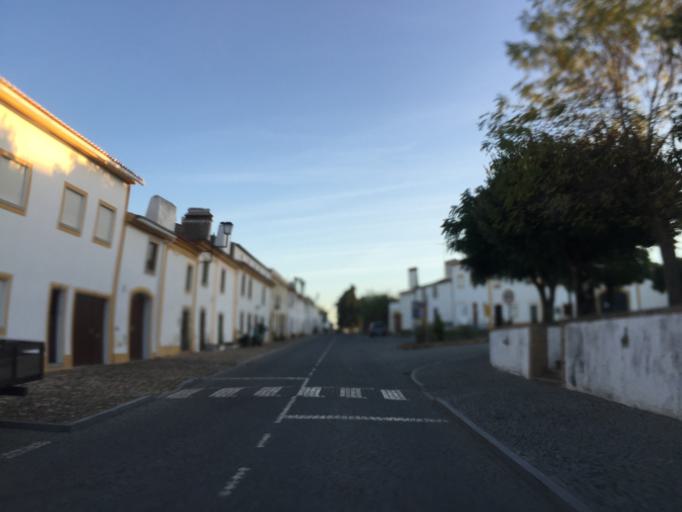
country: PT
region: Portalegre
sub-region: Alter do Chao
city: Alter do Chao
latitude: 39.3047
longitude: -7.6456
